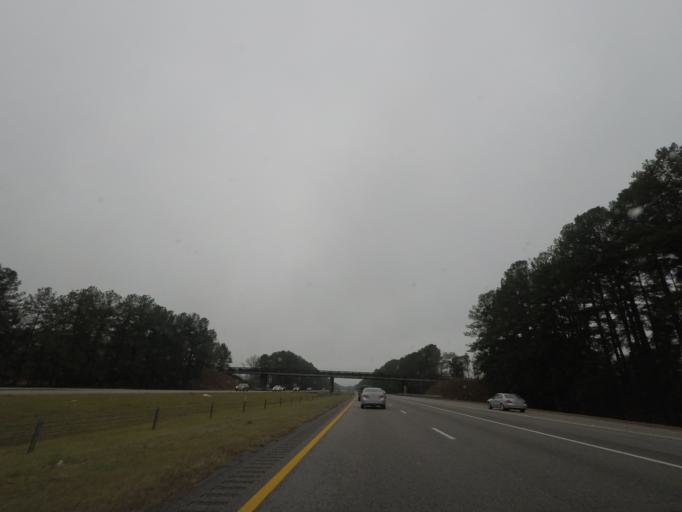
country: US
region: South Carolina
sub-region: Florence County
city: Timmonsville
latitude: 33.9458
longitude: -80.0586
